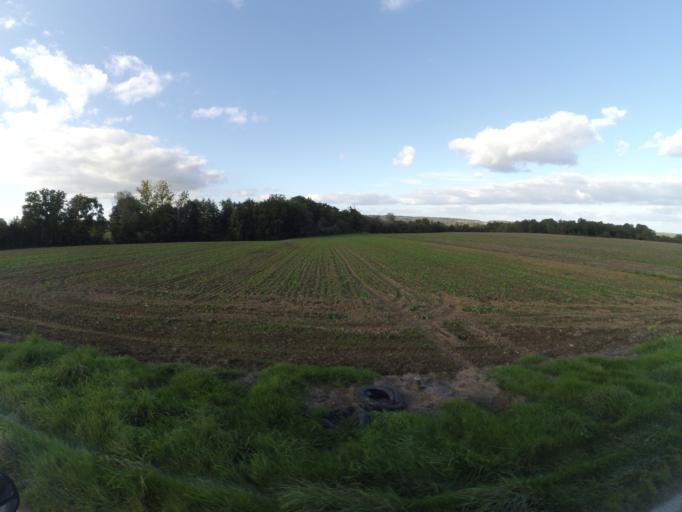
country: FR
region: Brittany
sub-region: Departement du Morbihan
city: Saint-Vincent-sur-Oust
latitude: 47.7143
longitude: -2.1707
